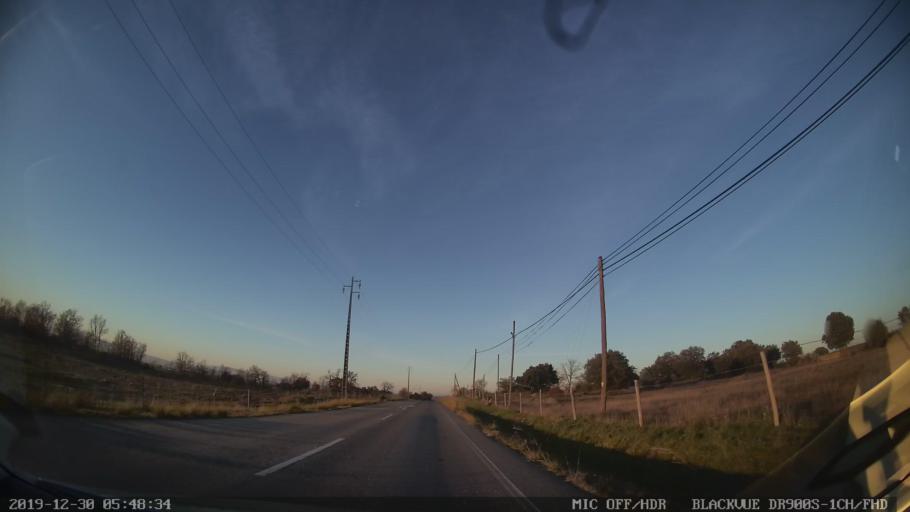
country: PT
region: Castelo Branco
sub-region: Idanha-A-Nova
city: Idanha-a-Nova
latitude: 39.9642
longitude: -7.2432
